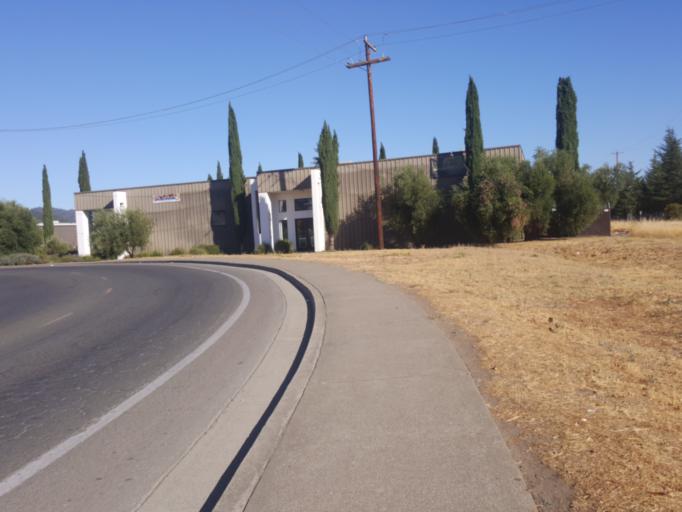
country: US
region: California
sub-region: Mendocino County
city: Ukiah
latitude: 39.1339
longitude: -123.2007
